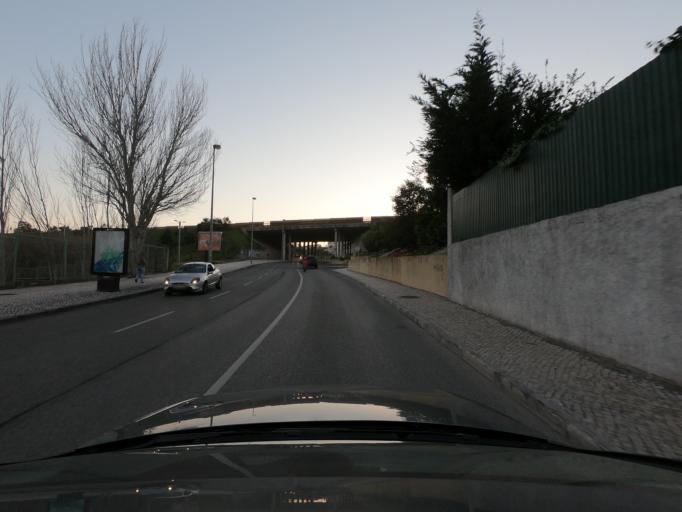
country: PT
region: Lisbon
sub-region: Sintra
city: Queluz
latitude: 38.7556
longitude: -9.2704
